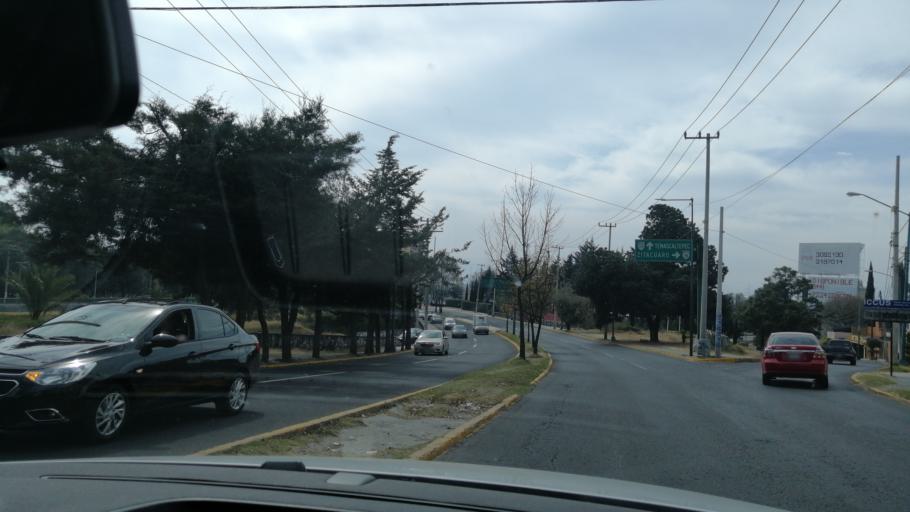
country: MX
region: Mexico
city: San Buenaventura
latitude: 19.2888
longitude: -99.6796
